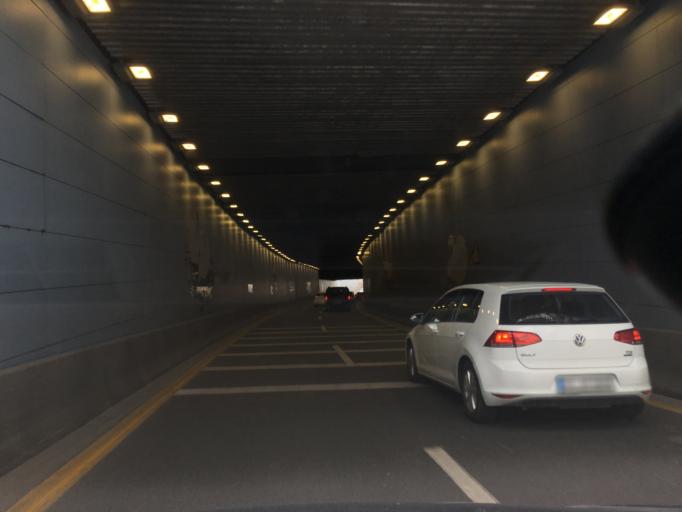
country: TR
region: Ankara
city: Cankaya
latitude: 39.9006
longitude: 32.8599
